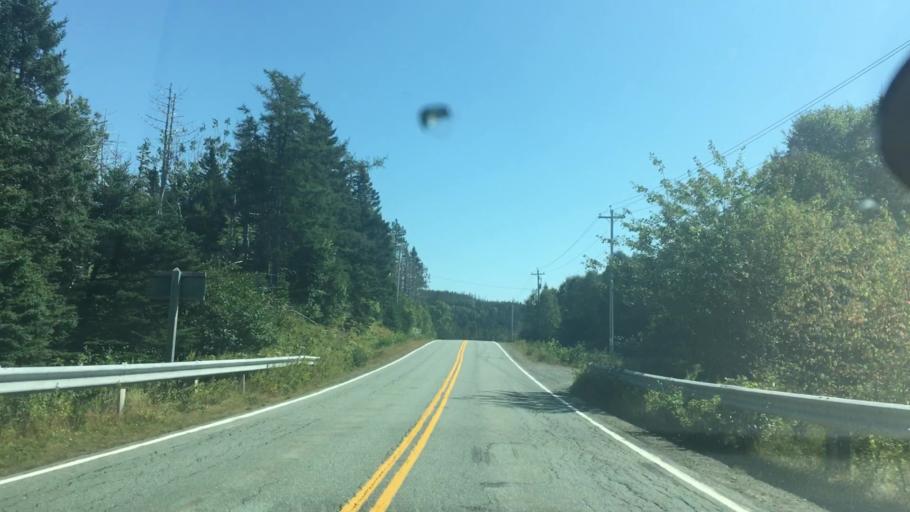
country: CA
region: Nova Scotia
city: Antigonish
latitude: 45.0128
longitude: -62.0965
